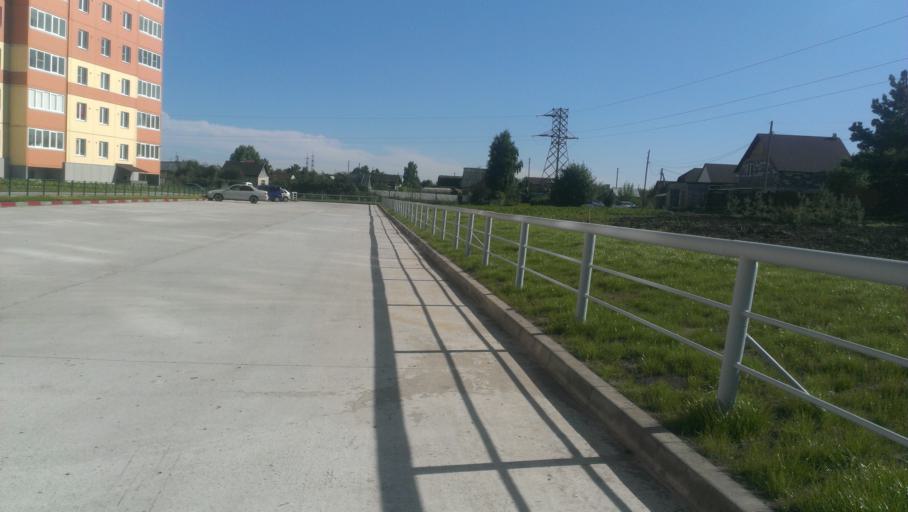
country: RU
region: Altai Krai
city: Novosilikatnyy
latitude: 53.3268
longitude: 83.6673
